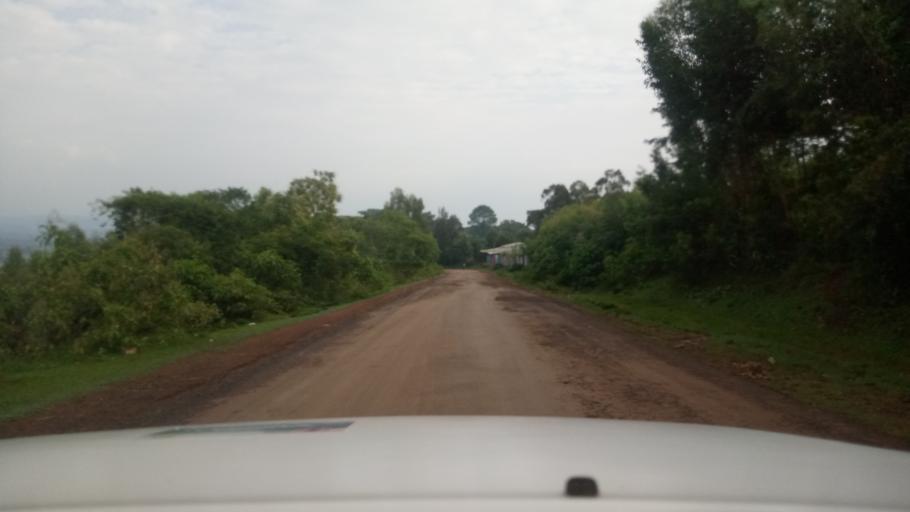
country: ET
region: Oromiya
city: Agaro
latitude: 7.7957
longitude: 36.7221
